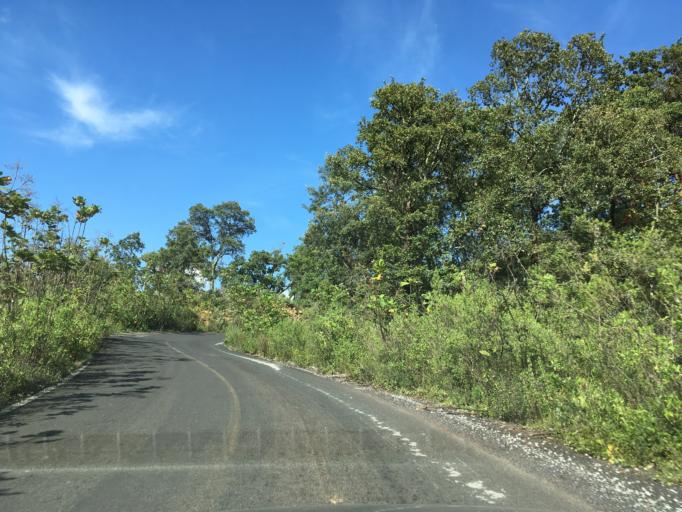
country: MX
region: Michoacan
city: Capula
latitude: 19.7449
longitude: -101.7966
